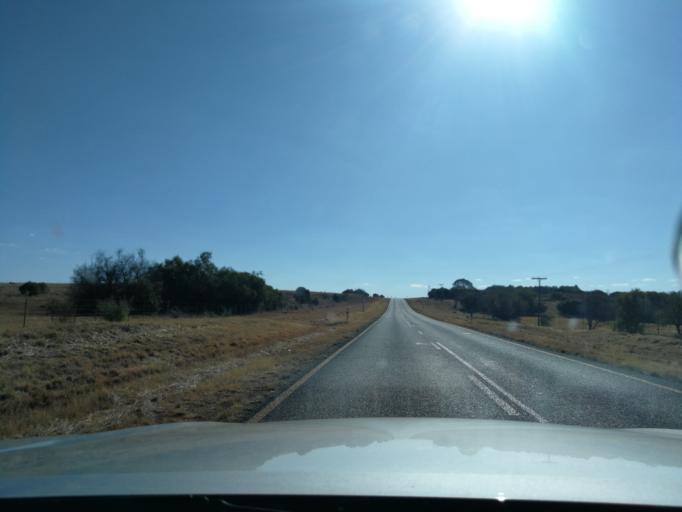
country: ZA
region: North-West
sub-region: Ngaka Modiri Molema District Municipality
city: Zeerust
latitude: -25.8033
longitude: 26.0314
